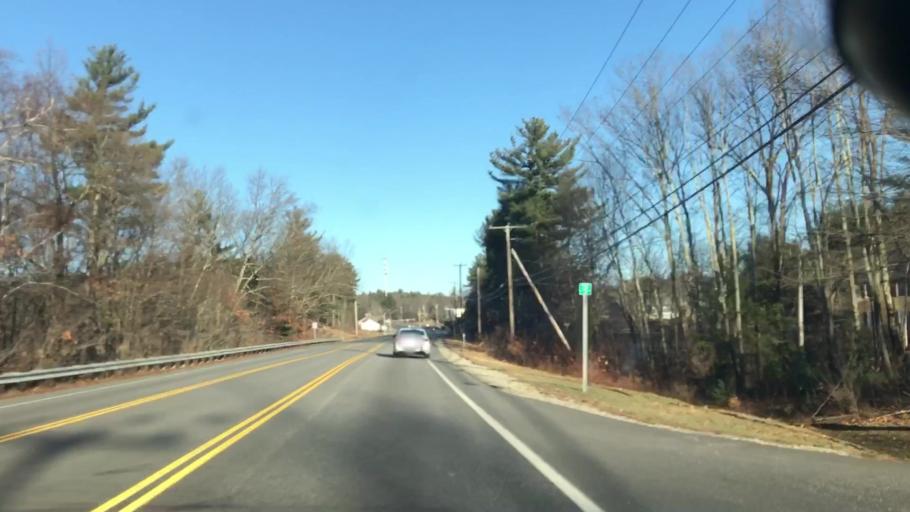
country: US
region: New Hampshire
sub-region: Hillsborough County
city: Bedford
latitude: 42.9193
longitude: -71.5423
